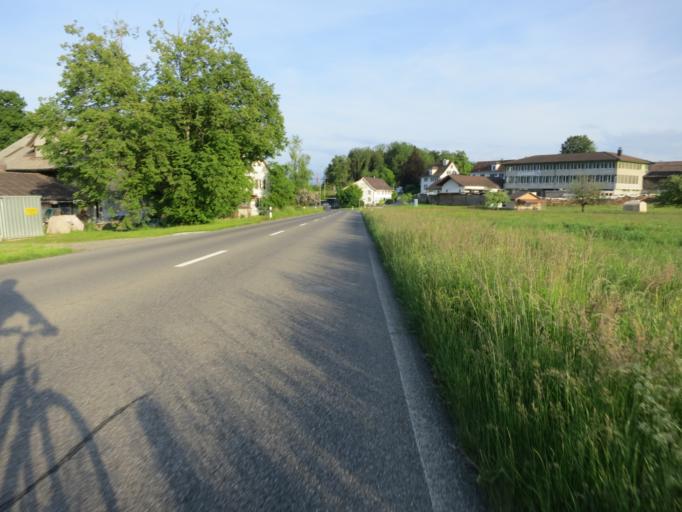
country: CH
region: Zurich
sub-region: Bezirk Hinwil
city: Bubikon
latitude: 47.2788
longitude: 8.8131
